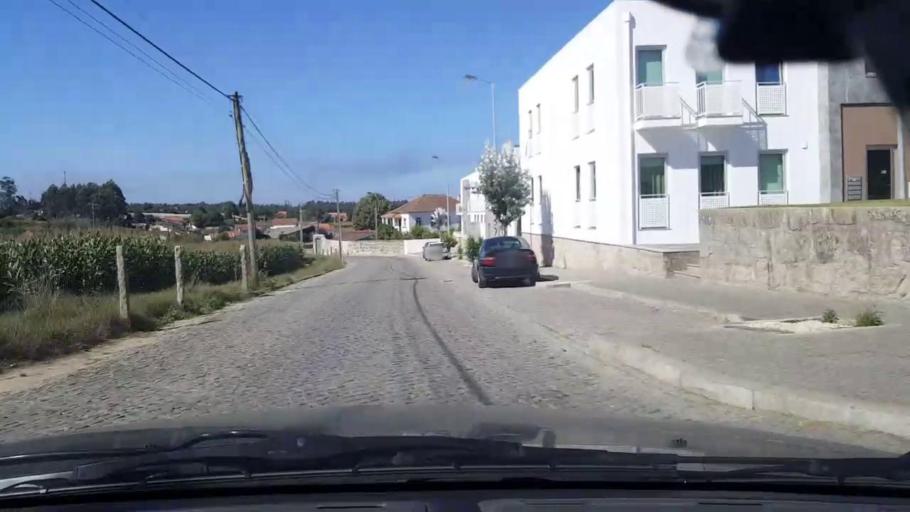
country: PT
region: Porto
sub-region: Maia
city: Gemunde
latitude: 41.2800
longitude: -8.6680
